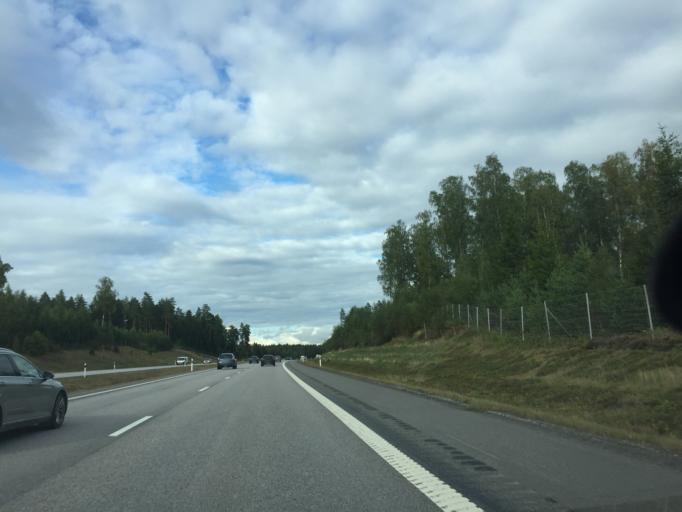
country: SE
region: OErebro
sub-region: Lindesbergs Kommun
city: Fellingsbro
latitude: 59.3654
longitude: 15.5759
